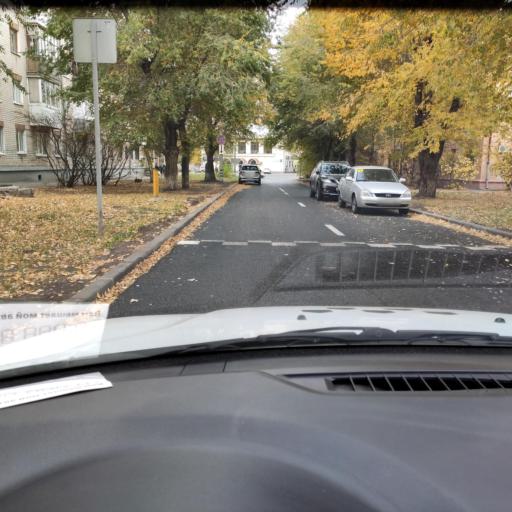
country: RU
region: Samara
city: Tol'yatti
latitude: 53.5113
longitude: 49.4124
